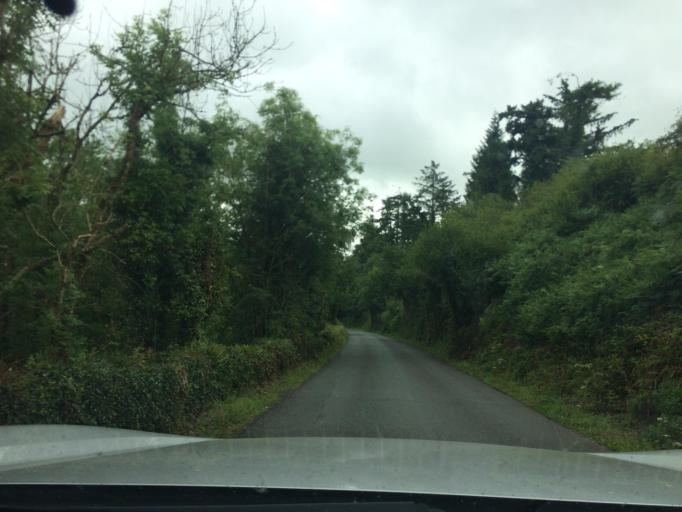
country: IE
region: Munster
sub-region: Waterford
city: Dungarvan
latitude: 52.1939
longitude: -7.7294
